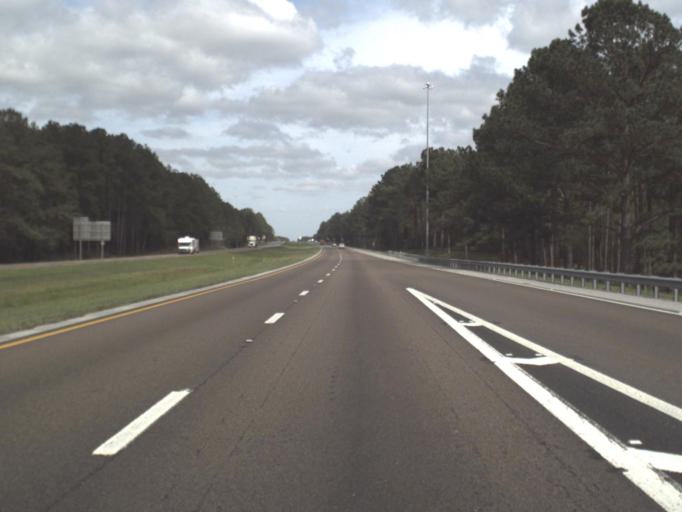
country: US
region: Florida
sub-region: Walton County
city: DeFuniak Springs
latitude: 30.6916
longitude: -86.1173
